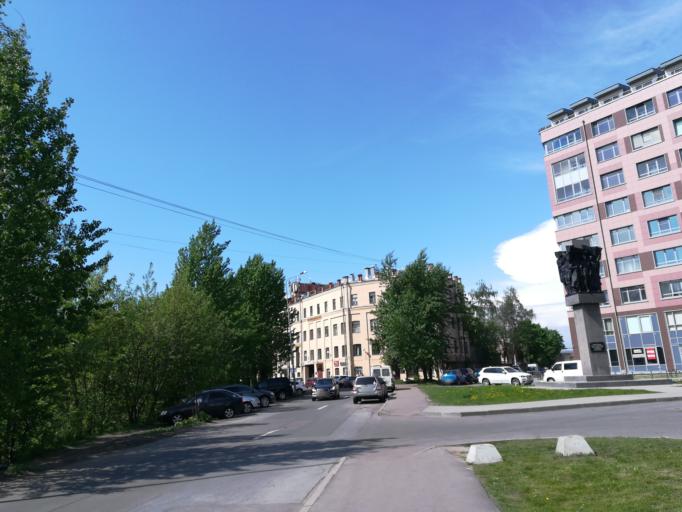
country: RU
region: St.-Petersburg
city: Vasyl'evsky Ostrov
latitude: 59.9485
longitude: 30.2634
